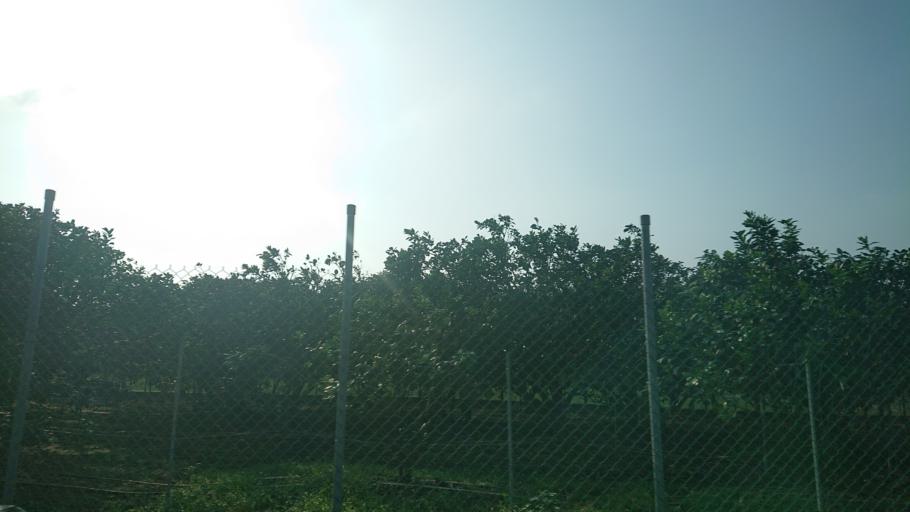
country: TW
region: Taiwan
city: Xinying
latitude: 23.1978
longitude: 120.2716
